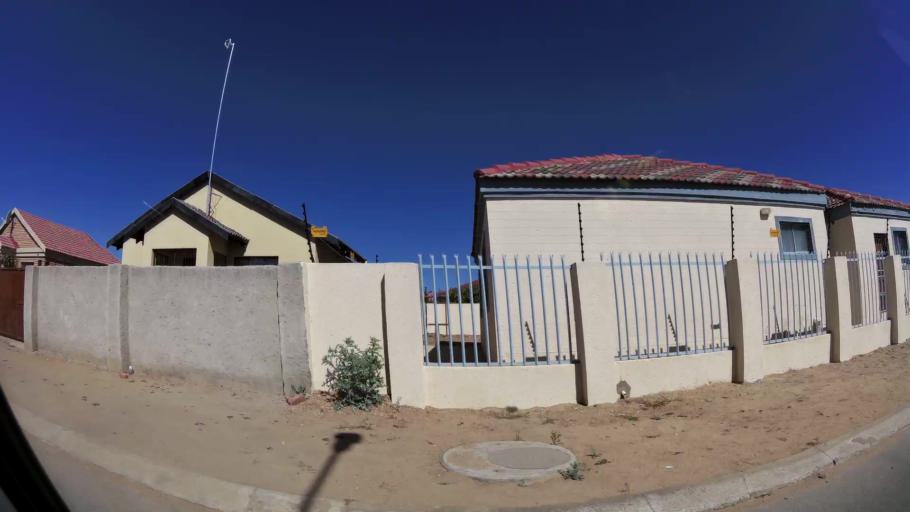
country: ZA
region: Limpopo
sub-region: Capricorn District Municipality
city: Polokwane
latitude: -23.8691
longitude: 29.4196
